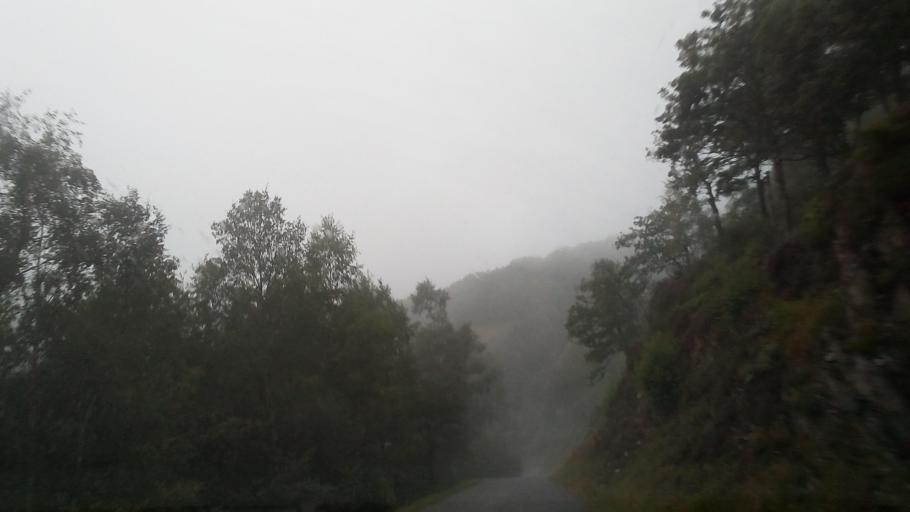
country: FR
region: Midi-Pyrenees
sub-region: Departement des Hautes-Pyrenees
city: Saint-Lary-Soulan
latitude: 42.8908
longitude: 0.3191
